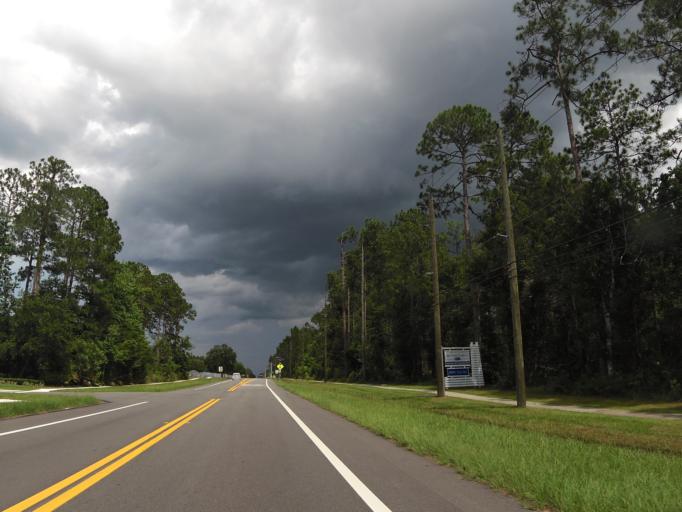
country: US
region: Florida
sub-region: Saint Johns County
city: Fruit Cove
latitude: 30.0624
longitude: -81.6513
